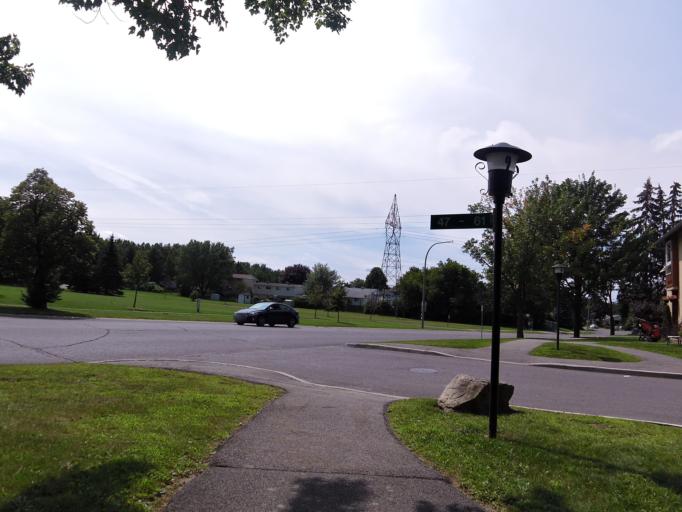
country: CA
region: Ontario
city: Ottawa
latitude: 45.3366
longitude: -75.7314
